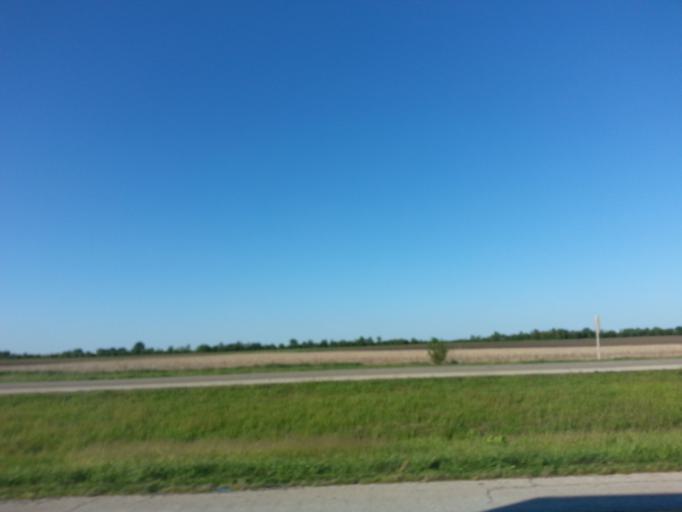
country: US
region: Illinois
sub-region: McLean County
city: Le Roy
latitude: 40.3162
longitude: -88.7330
